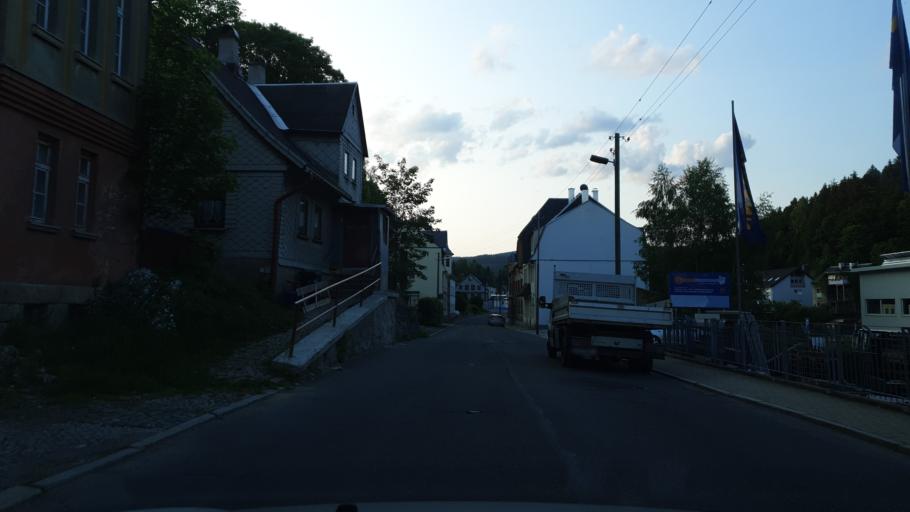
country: DE
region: Saxony
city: Klingenthal
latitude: 50.3613
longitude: 12.4682
